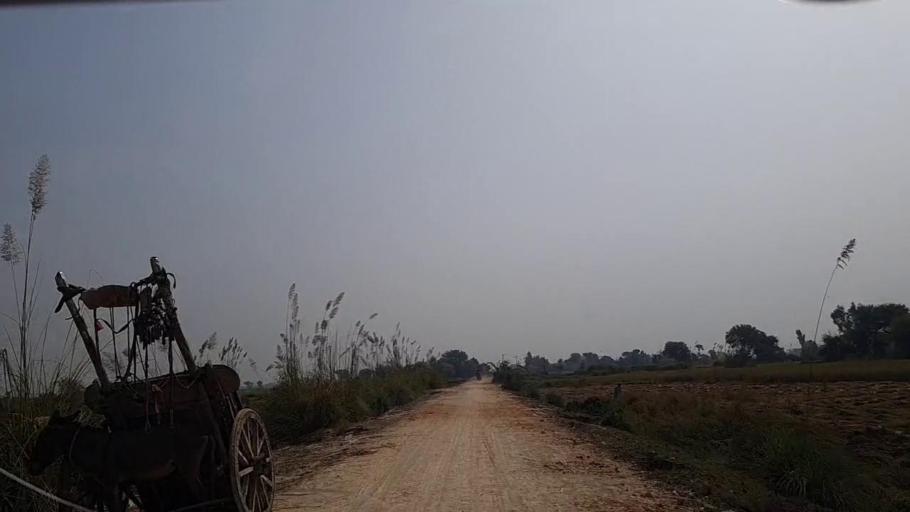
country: PK
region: Sindh
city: Garhi Yasin
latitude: 27.9249
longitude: 68.5669
